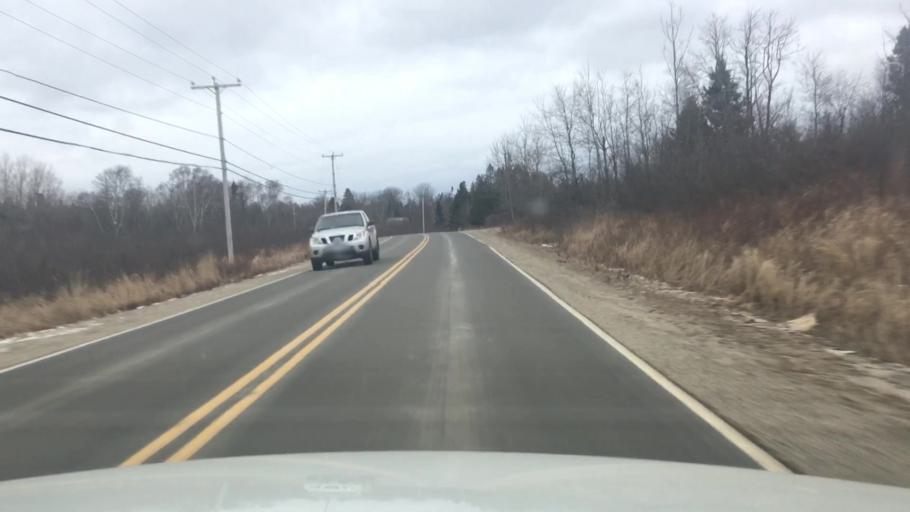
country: US
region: Maine
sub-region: Washington County
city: Jonesport
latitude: 44.5555
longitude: -67.6260
